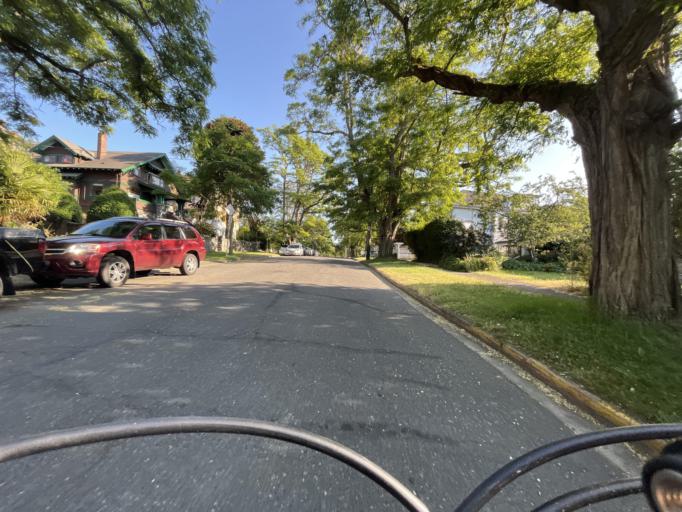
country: CA
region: British Columbia
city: Victoria
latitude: 48.4233
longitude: -123.3448
